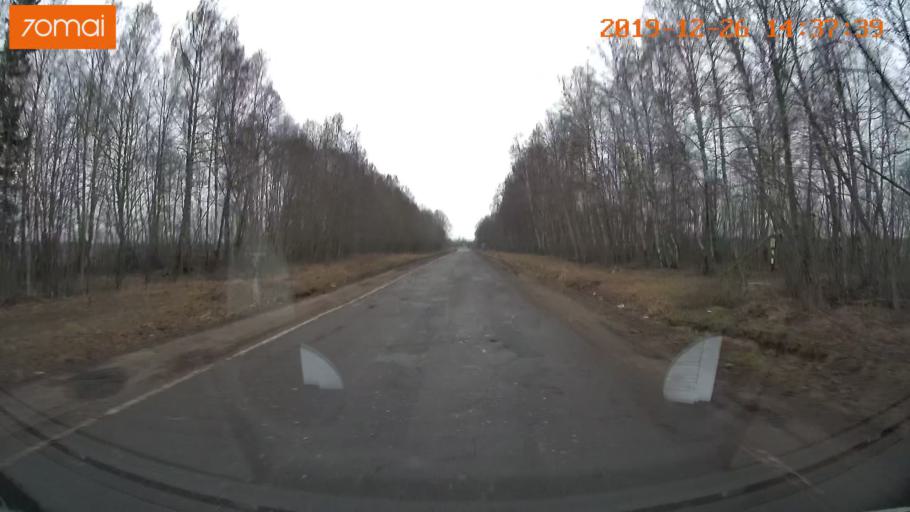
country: RU
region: Jaroslavl
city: Poshekhon'ye
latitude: 58.4006
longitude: 38.9717
